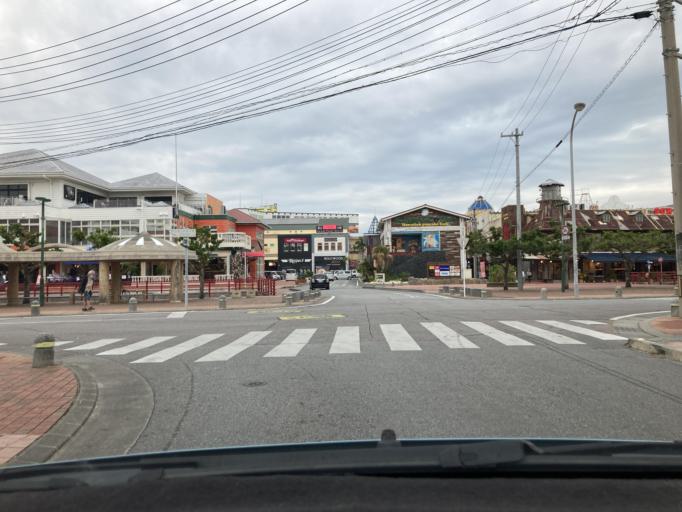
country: JP
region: Okinawa
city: Chatan
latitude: 26.3153
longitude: 127.7563
